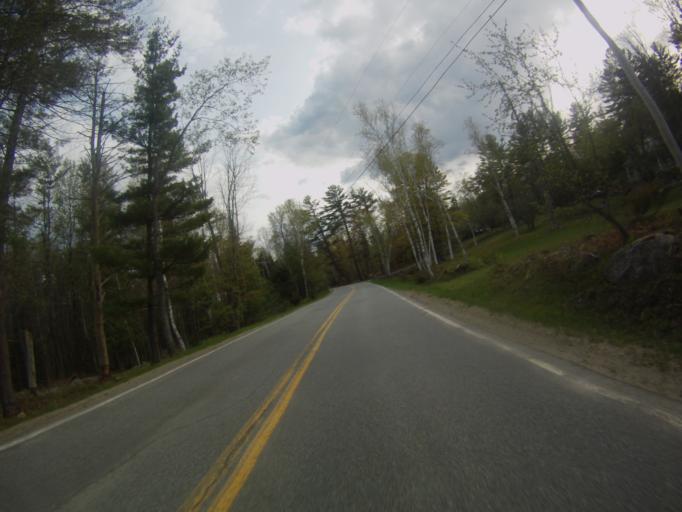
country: US
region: New York
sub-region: Warren County
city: Warrensburg
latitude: 43.8332
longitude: -73.8973
